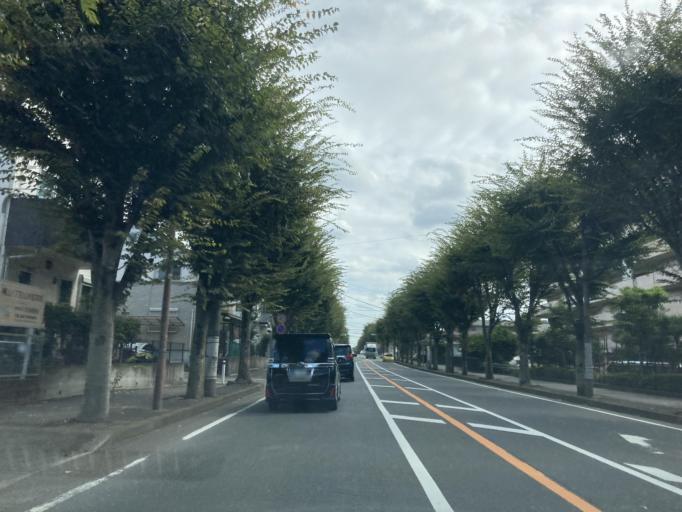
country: JP
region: Kanagawa
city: Zama
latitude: 35.5678
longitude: 139.3642
